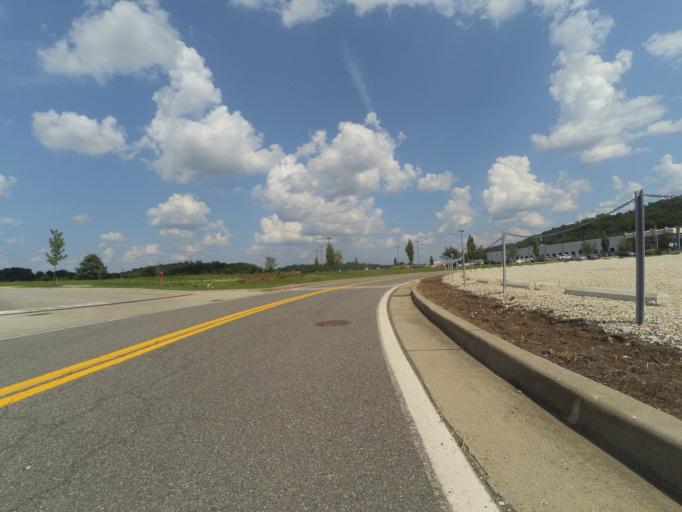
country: US
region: West Virginia
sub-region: Cabell County
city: Huntington
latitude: 38.3950
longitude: -82.4219
